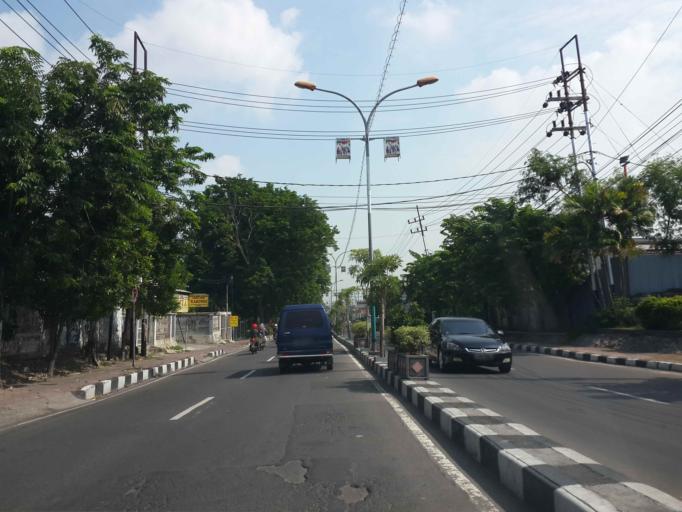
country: ID
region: East Java
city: Kebomas
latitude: -7.1808
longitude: 112.6496
